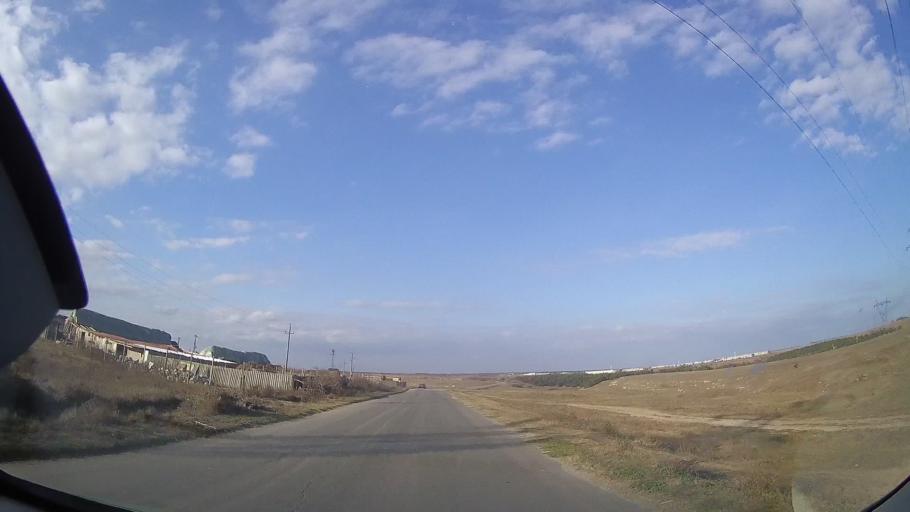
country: RO
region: Constanta
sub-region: Comuna Limanu
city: Limanu
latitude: 43.8031
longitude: 28.5215
